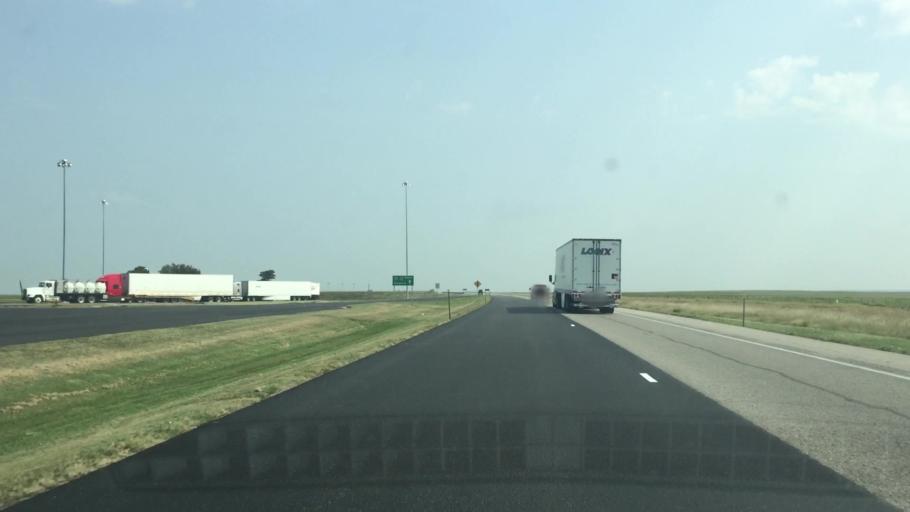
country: US
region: Kansas
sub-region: Chase County
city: Cottonwood Falls
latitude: 38.0955
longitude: -96.5785
